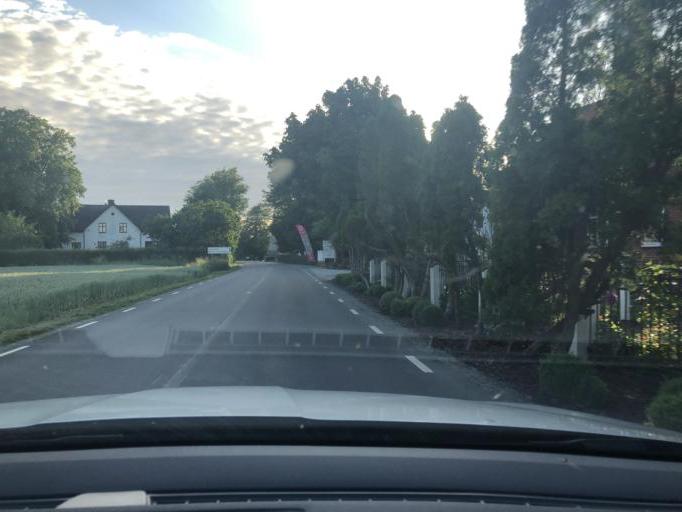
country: SE
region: Skane
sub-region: Ystads Kommun
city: Kopingebro
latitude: 55.4279
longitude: 14.1525
